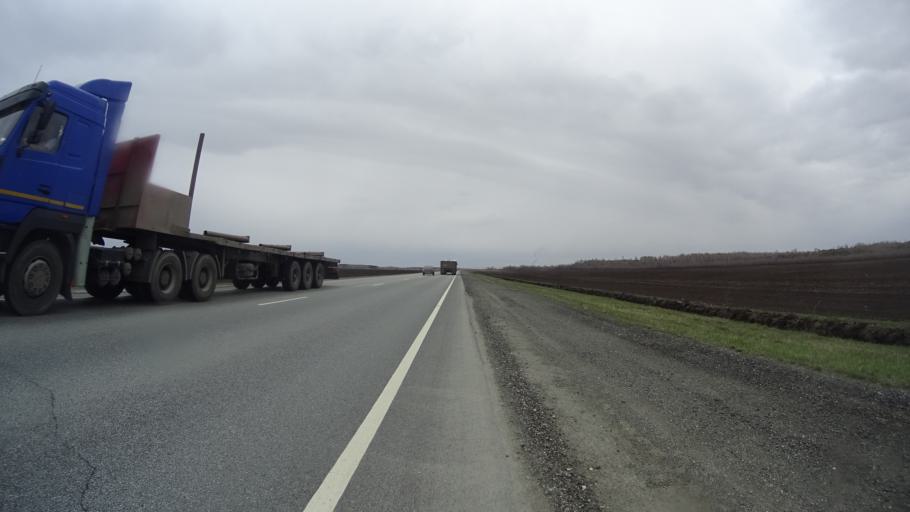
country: RU
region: Chelyabinsk
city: Krasnogorskiy
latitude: 54.5741
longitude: 61.2911
